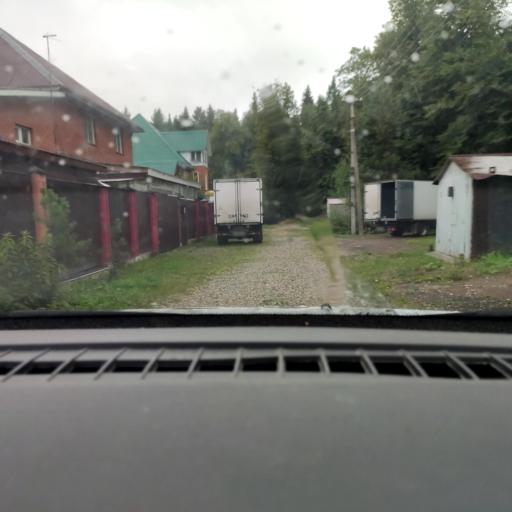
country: RU
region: Perm
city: Ferma
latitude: 57.9434
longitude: 56.4133
